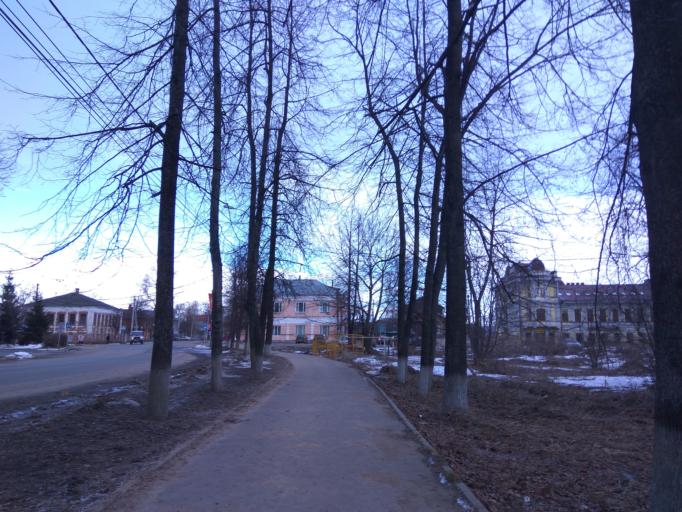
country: RU
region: Jaroslavl
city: Rostov
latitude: 57.1871
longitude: 39.4264
